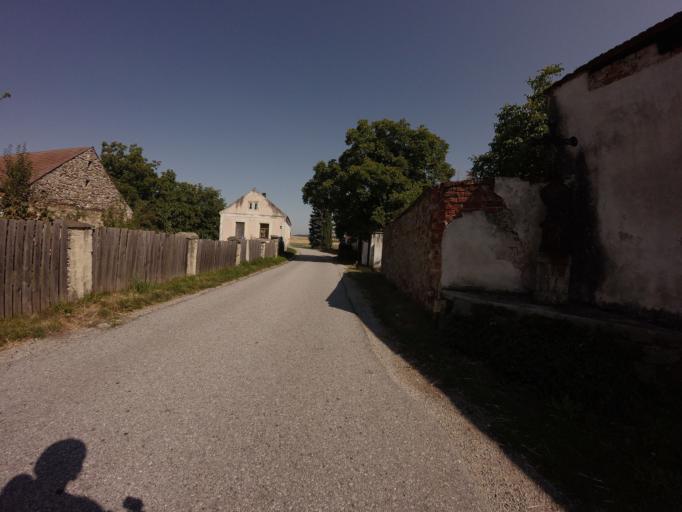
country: CZ
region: Jihocesky
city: Kamenny Ujezd
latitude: 48.8659
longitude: 14.3787
